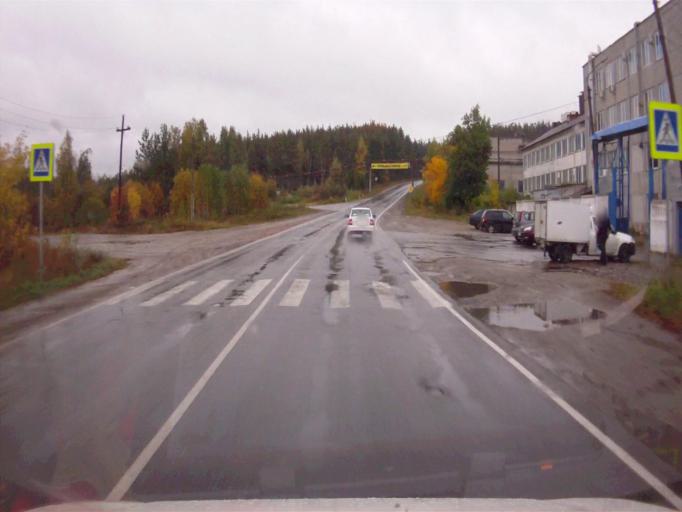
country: RU
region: Chelyabinsk
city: Kyshtym
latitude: 55.7284
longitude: 60.5193
